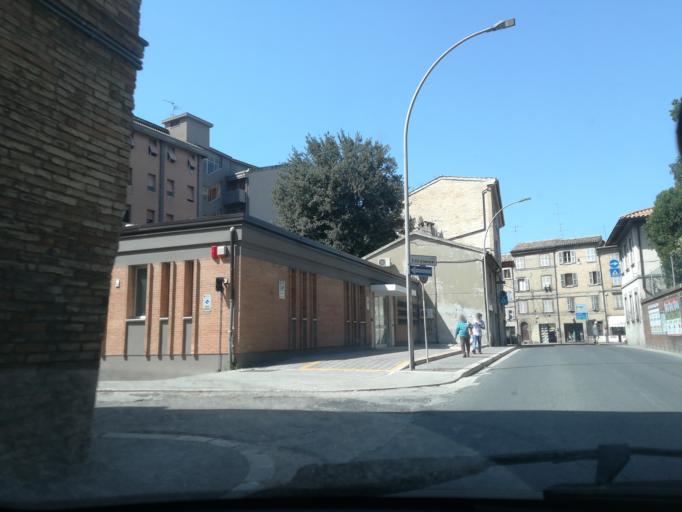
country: IT
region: The Marches
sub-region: Provincia di Macerata
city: Macerata
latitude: 43.2952
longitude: 13.4570
